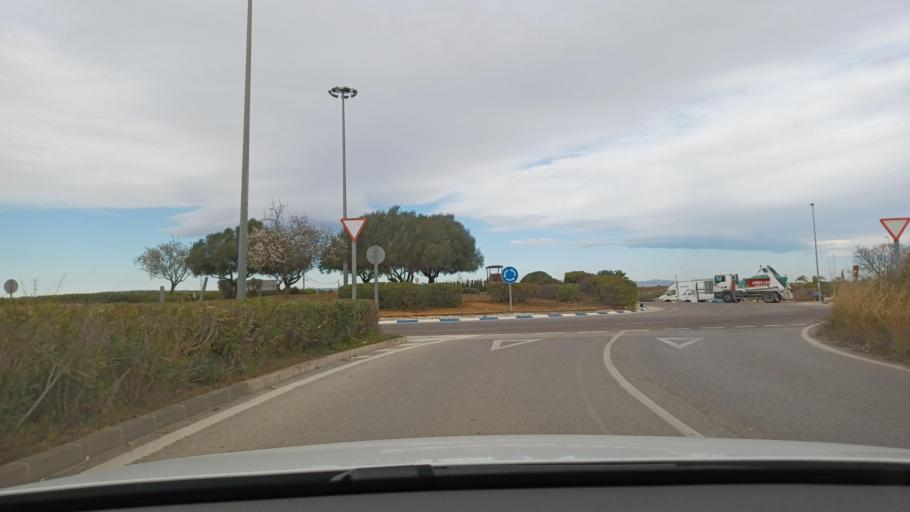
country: ES
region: Valencia
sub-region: Provincia de Valencia
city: Picassent
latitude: 39.3684
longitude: -0.4603
